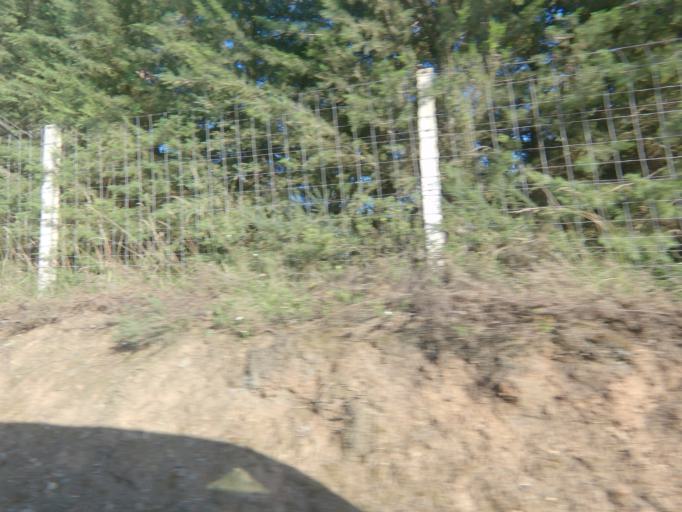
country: PT
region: Vila Real
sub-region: Sabrosa
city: Vilela
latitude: 41.2473
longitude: -7.6043
